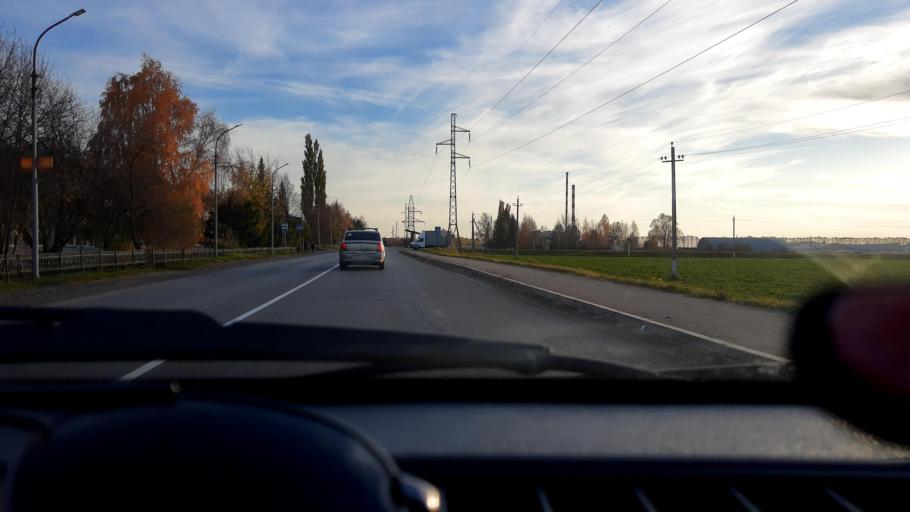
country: RU
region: Bashkortostan
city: Ufa
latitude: 54.8316
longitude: 55.9948
